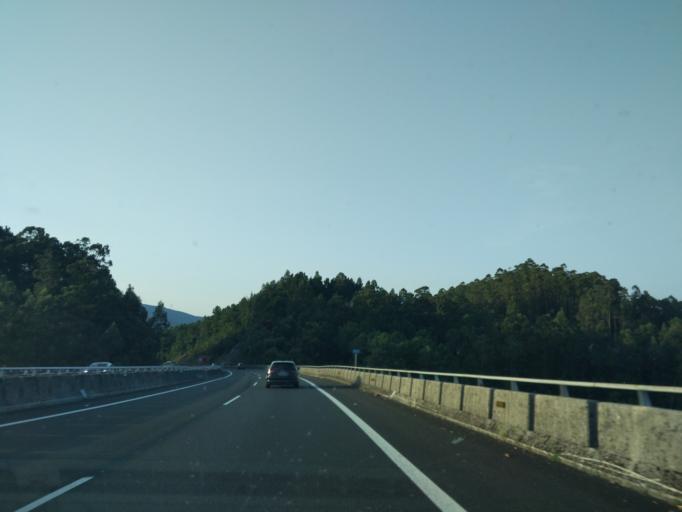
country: ES
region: Galicia
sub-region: Provincia de Pontevedra
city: Portas
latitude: 42.5764
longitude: -8.6730
